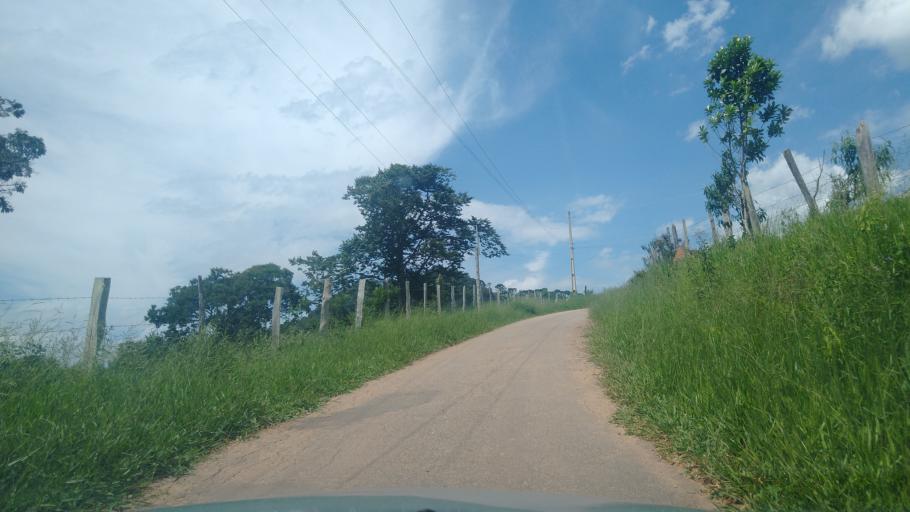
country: BR
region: Minas Gerais
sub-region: Extrema
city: Extrema
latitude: -22.7579
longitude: -46.2882
